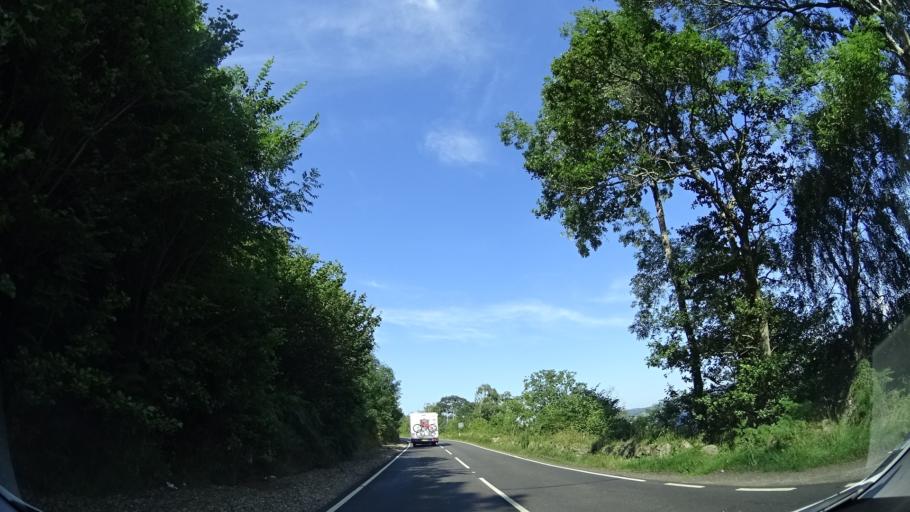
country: GB
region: Scotland
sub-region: Highland
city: Beauly
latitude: 57.3697
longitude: -4.3877
